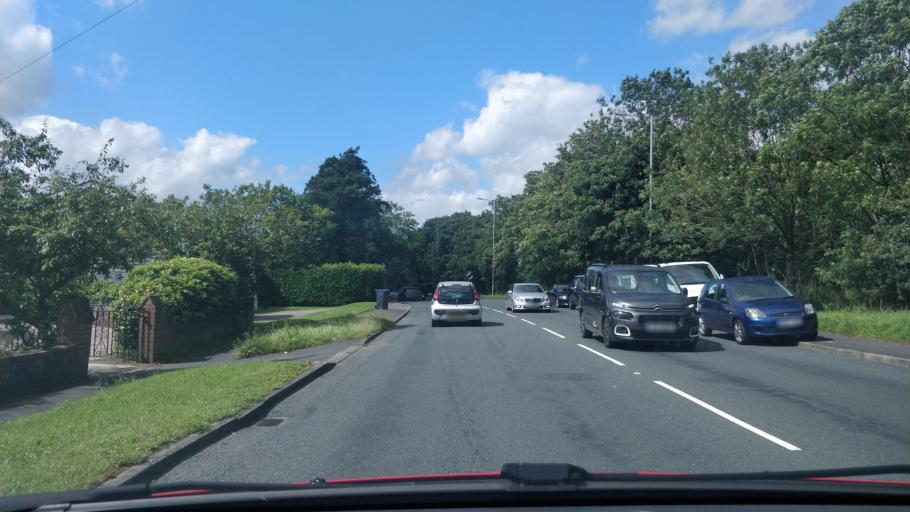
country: GB
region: England
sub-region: Lancashire
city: Appley Bridge
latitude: 53.5929
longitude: -2.7288
